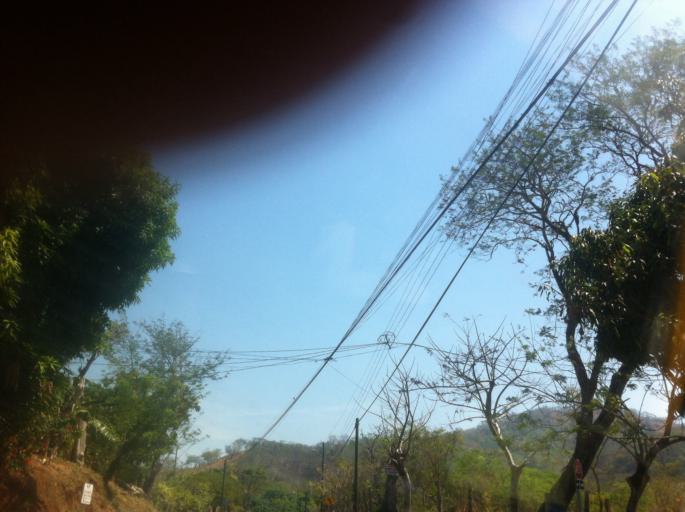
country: CR
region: Guanacaste
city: Hojancha
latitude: 10.0687
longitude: -85.4726
